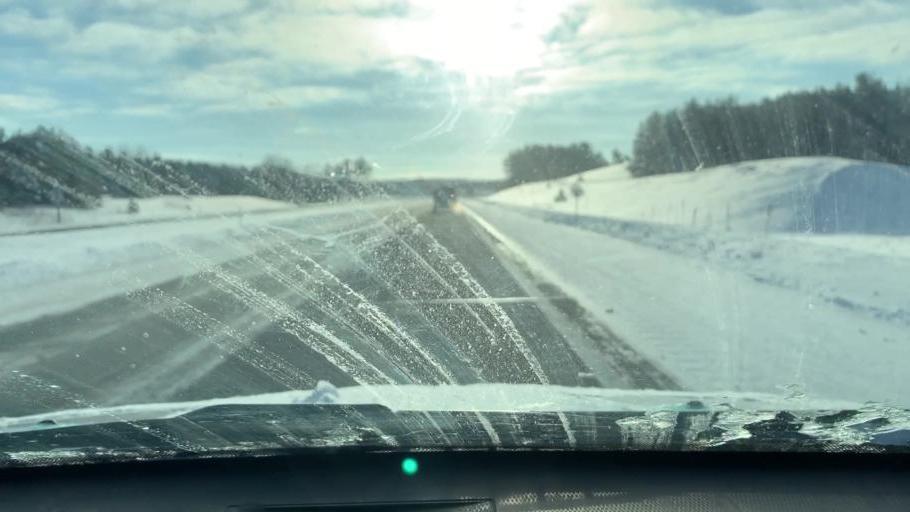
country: US
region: Michigan
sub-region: Wexford County
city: Cadillac
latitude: 44.2568
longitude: -85.3780
